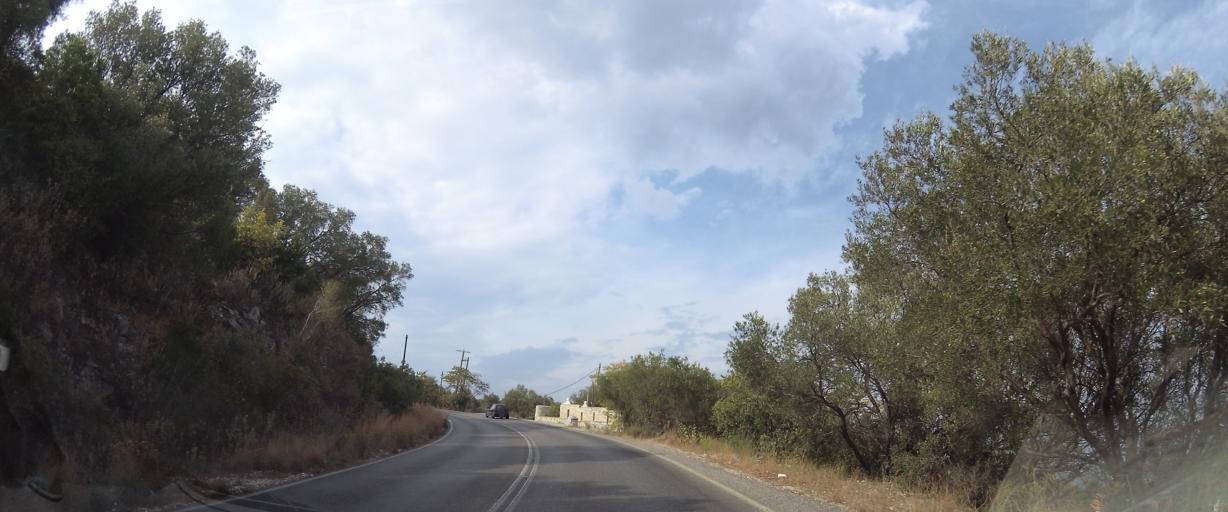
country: GR
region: Ionian Islands
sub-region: Nomos Kerkyras
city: Acharavi
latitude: 39.8012
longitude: 19.8800
